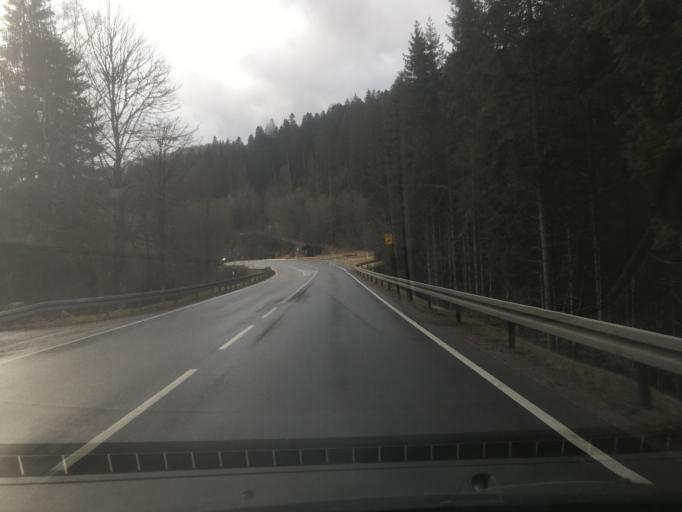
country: DE
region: Baden-Wuerttemberg
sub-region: Freiburg Region
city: Schluchsee
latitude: 47.7881
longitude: 8.1812
